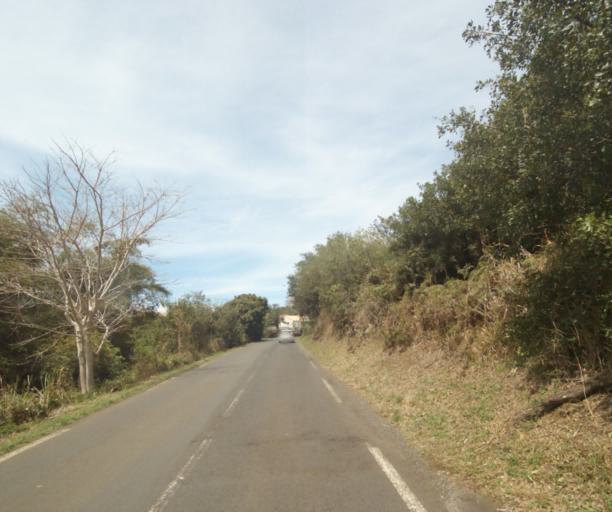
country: RE
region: Reunion
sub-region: Reunion
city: Saint-Paul
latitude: -21.0482
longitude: 55.2775
